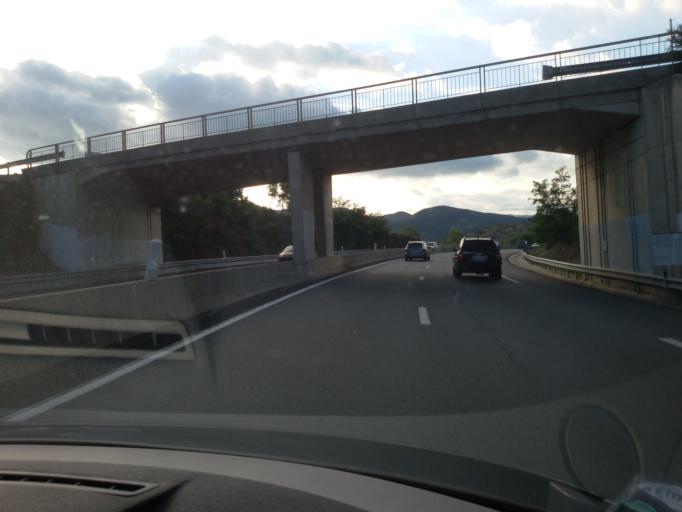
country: FR
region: Languedoc-Roussillon
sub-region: Departement de l'Herault
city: Lodeve
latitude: 43.6930
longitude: 3.3445
